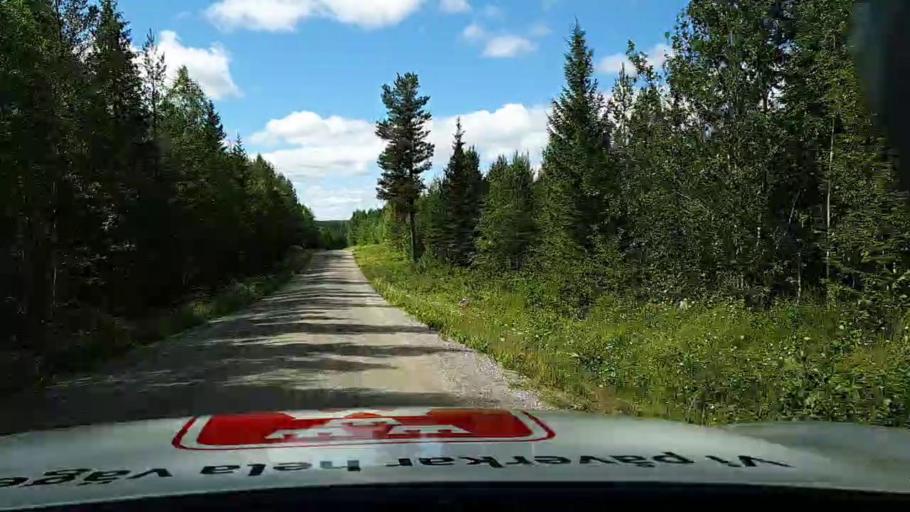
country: SE
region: Jaemtland
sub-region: Braecke Kommun
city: Braecke
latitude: 62.7385
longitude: 15.4910
